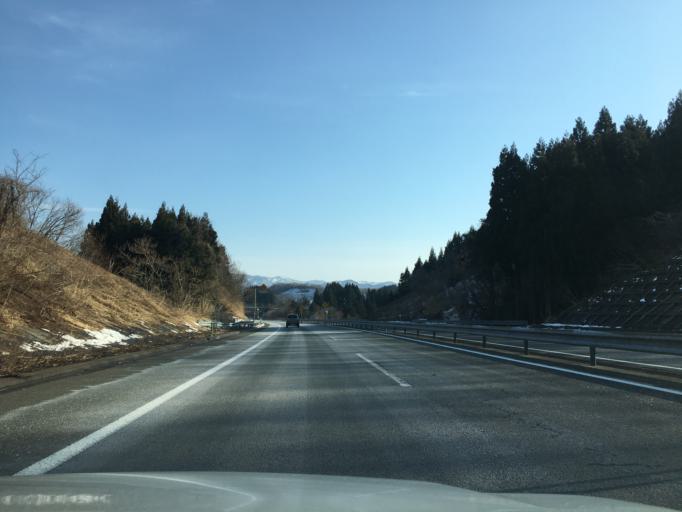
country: JP
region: Yamagata
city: Tsuruoka
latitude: 38.6384
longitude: 139.8303
